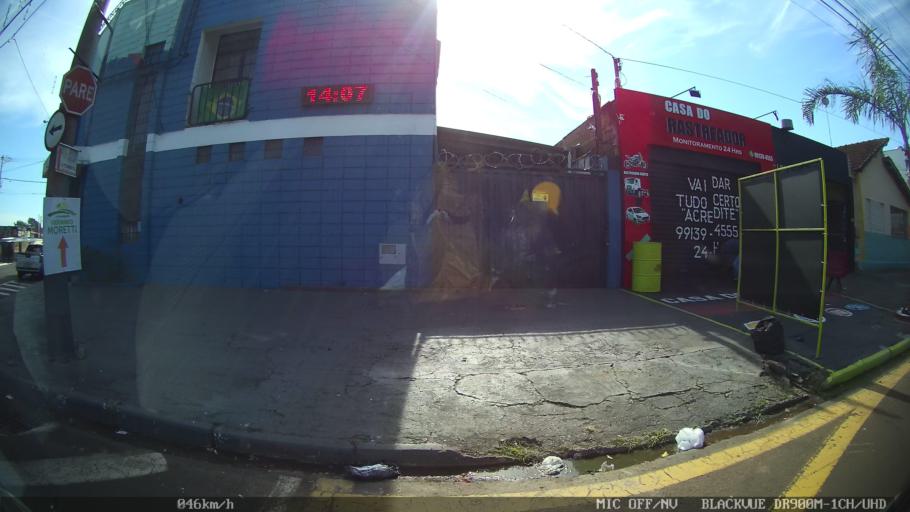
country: BR
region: Sao Paulo
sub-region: Franca
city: Franca
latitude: -20.5397
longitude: -47.4176
